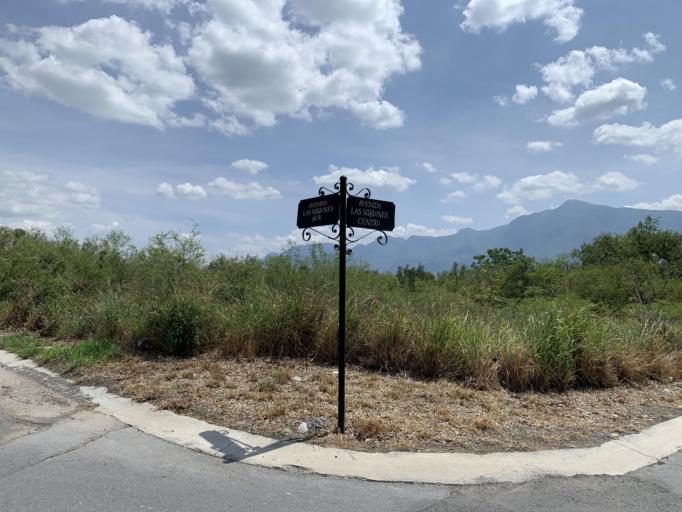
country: MX
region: Nuevo Leon
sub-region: Juarez
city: Bosques de San Pedro
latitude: 25.5109
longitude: -100.1881
